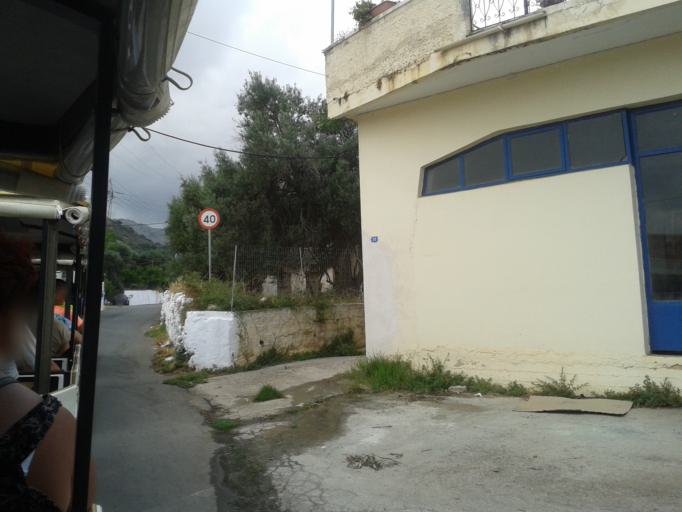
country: GR
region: Crete
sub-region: Nomos Chanias
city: Perivolia
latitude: 35.4794
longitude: 23.9935
